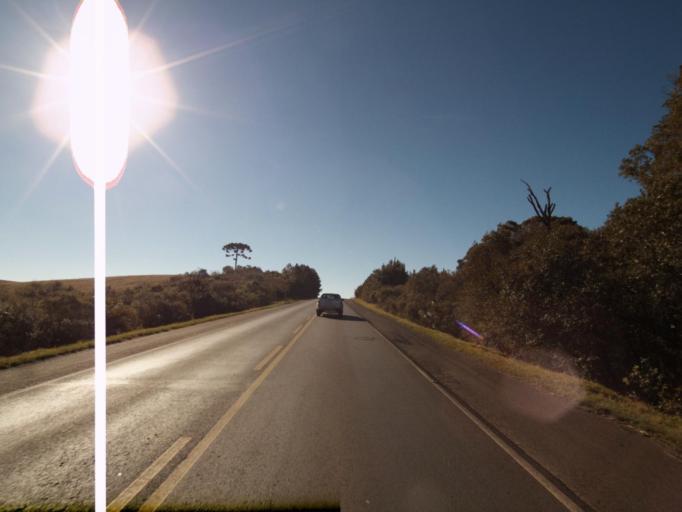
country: BR
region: Santa Catarina
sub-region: Concordia
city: Concordia
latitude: -26.9192
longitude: -51.9325
